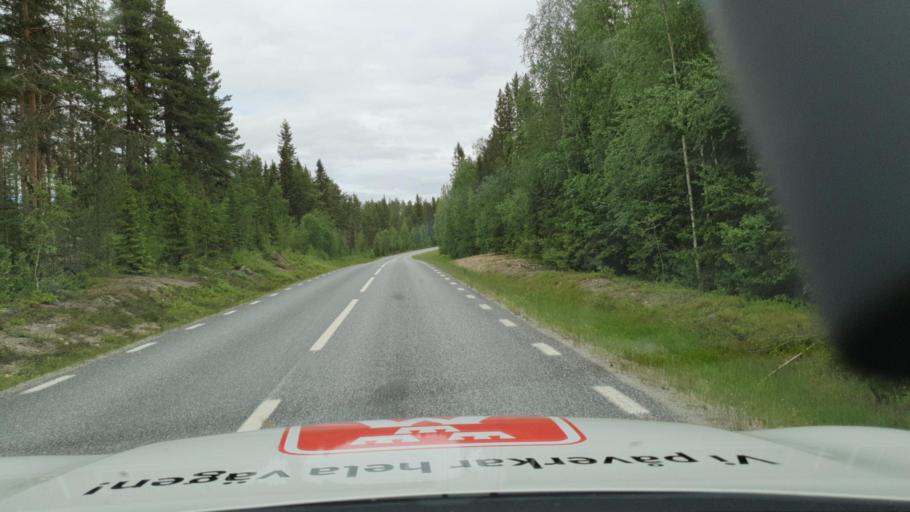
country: SE
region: Vaesterbotten
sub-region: Asele Kommun
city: Insjon
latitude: 64.2578
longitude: 17.5524
